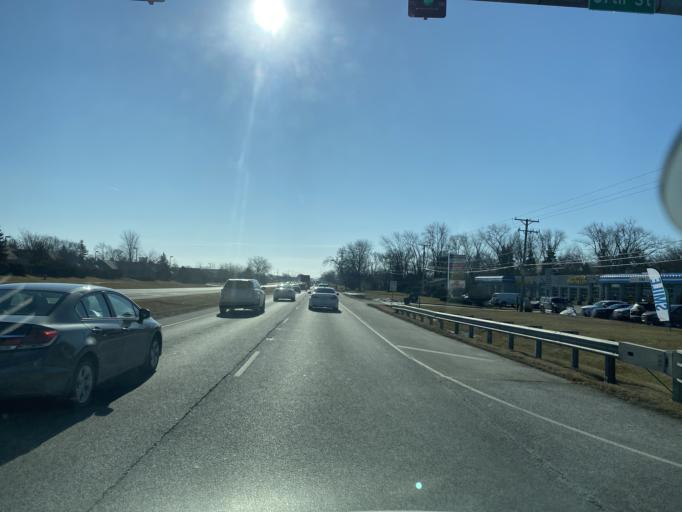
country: US
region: Illinois
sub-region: DuPage County
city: Willowbrook
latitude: 41.7670
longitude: -87.9453
